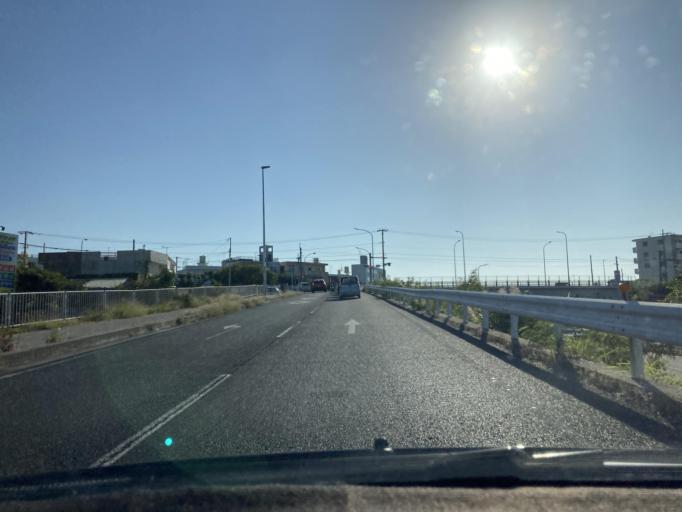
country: JP
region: Okinawa
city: Ginowan
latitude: 26.2497
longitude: 127.7177
